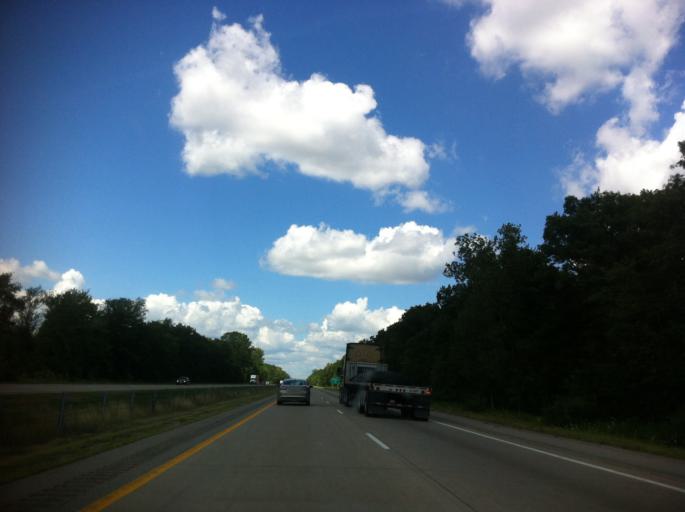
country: US
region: Michigan
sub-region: Monroe County
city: Petersburg
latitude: 41.8881
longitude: -83.6613
